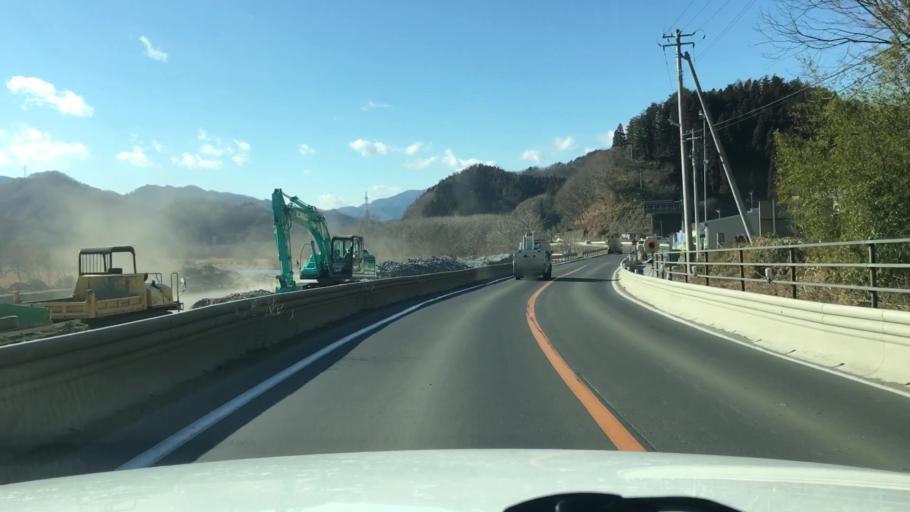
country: JP
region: Iwate
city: Miyako
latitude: 39.6323
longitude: 141.8888
